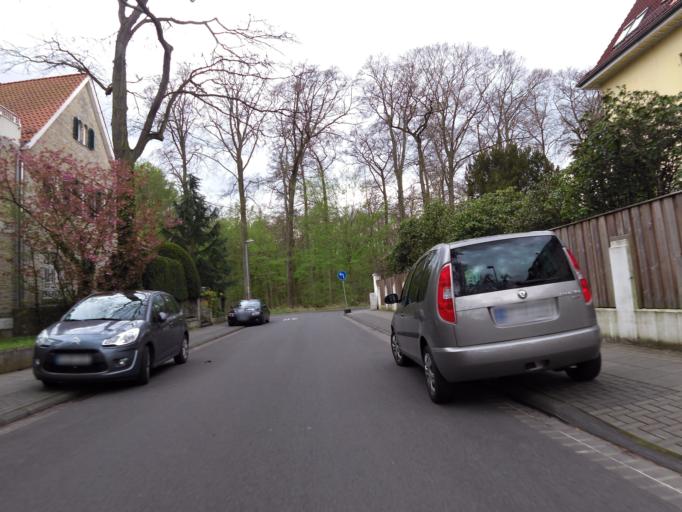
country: DE
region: Lower Saxony
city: Laatzen
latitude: 52.3697
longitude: 9.7924
